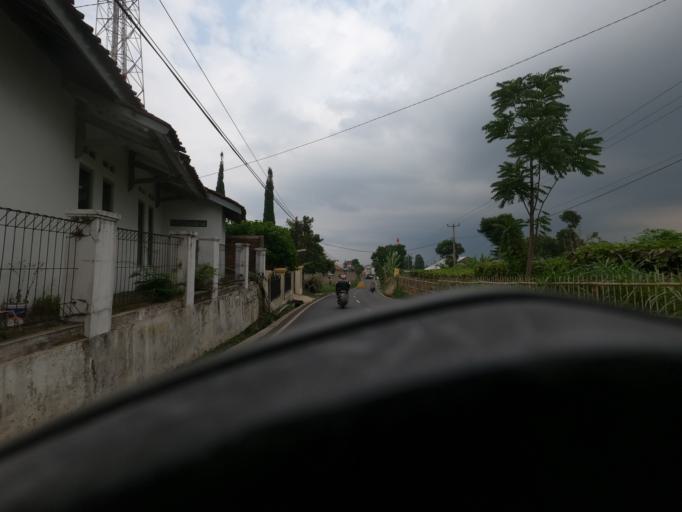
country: ID
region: West Java
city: Cimahi
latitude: -6.8218
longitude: 107.5352
